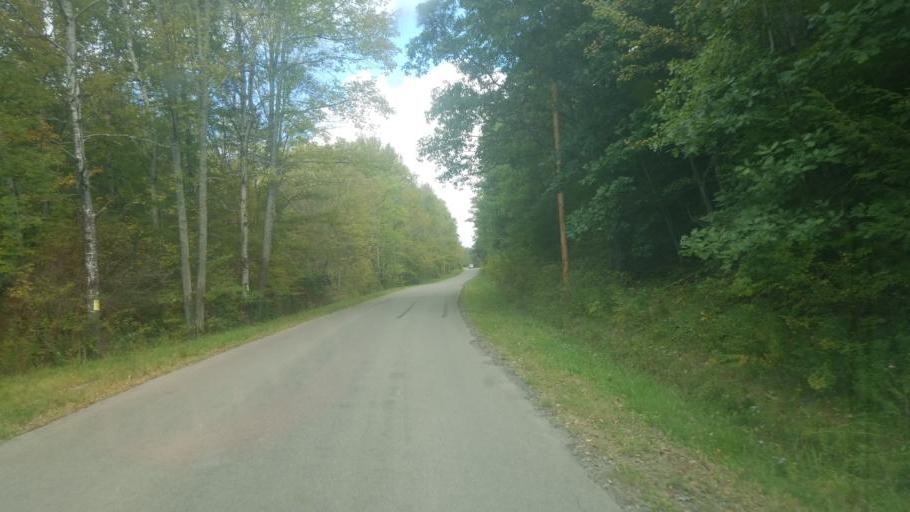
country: US
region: New York
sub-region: Cattaraugus County
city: Weston Mills
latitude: 42.1517
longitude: -78.3611
